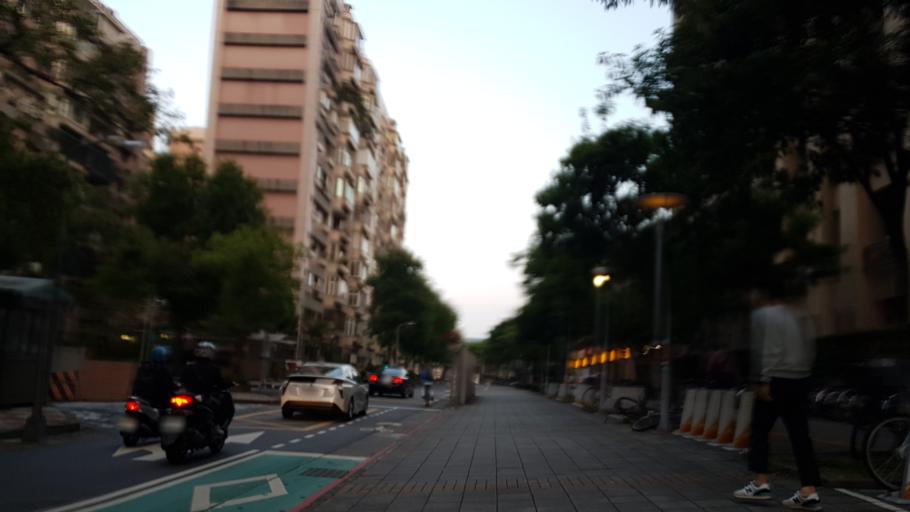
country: TW
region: Taipei
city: Taipei
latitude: 25.0152
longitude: 121.5301
